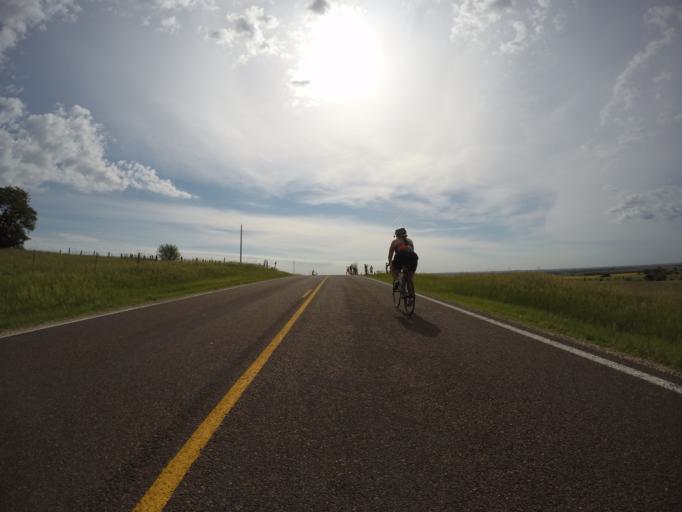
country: US
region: Kansas
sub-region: Washington County
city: Washington
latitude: 39.7122
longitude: -97.3038
